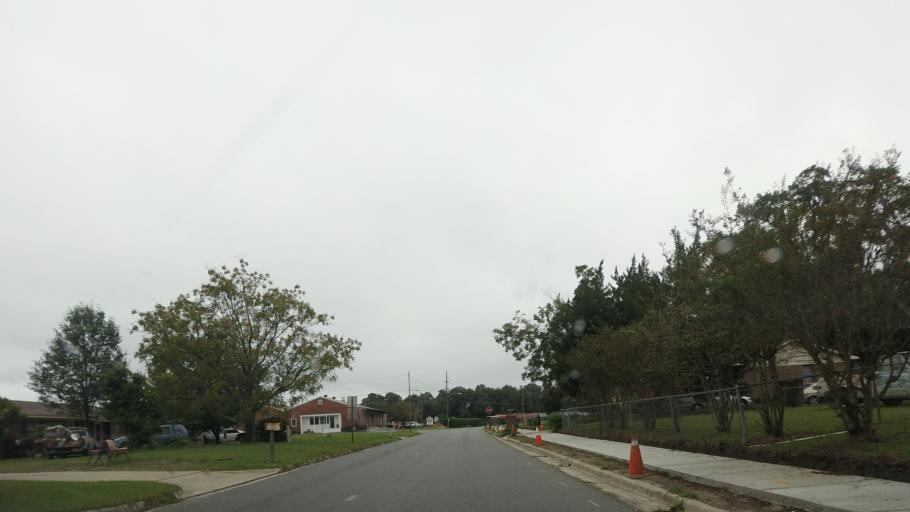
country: US
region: Georgia
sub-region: Lowndes County
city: Valdosta
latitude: 30.8193
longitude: -83.2772
